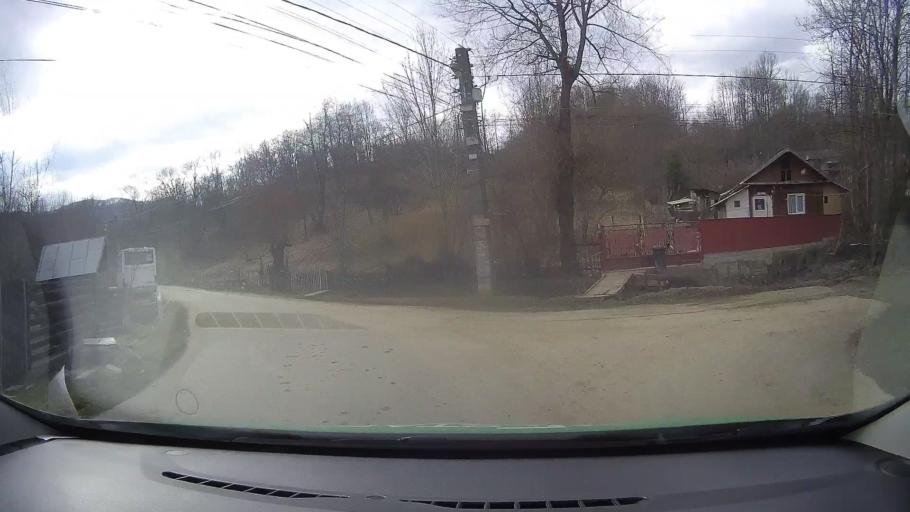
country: RO
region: Dambovita
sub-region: Comuna Visinesti
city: Visinesti
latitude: 45.1134
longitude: 25.5839
